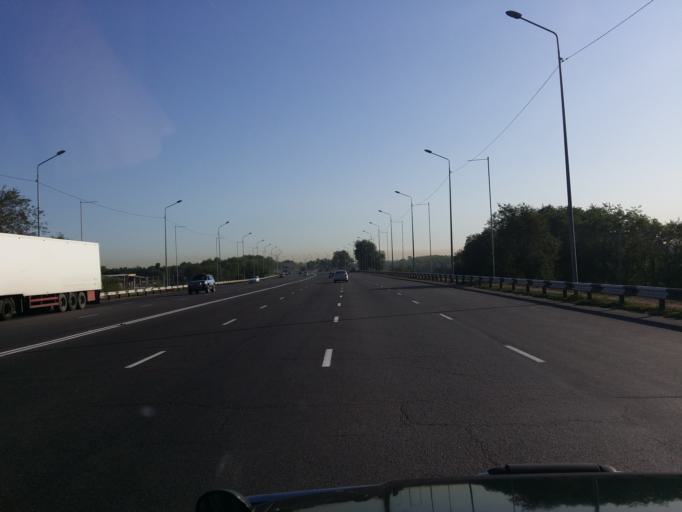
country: KZ
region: Almaty Oblysy
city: Pervomayskiy
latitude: 43.3478
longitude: 76.9347
